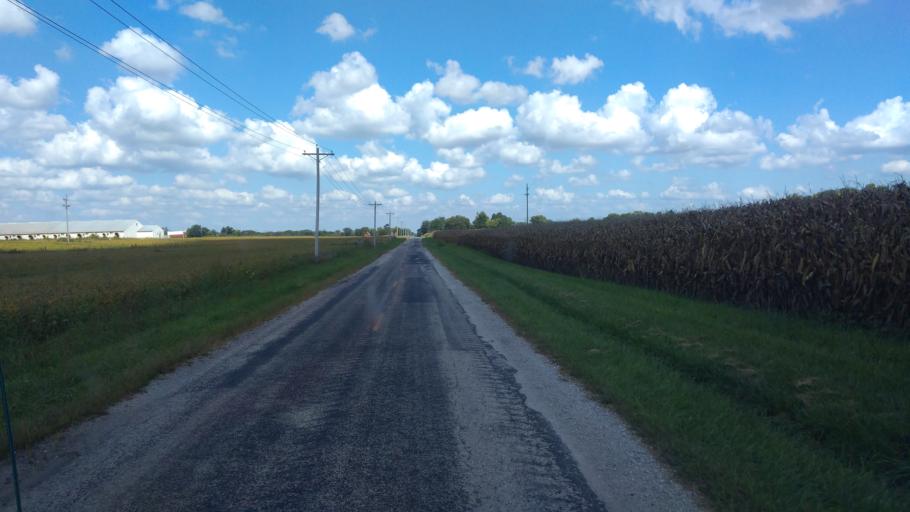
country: US
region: Ohio
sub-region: Wyandot County
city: Upper Sandusky
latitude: 40.6602
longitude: -83.3429
